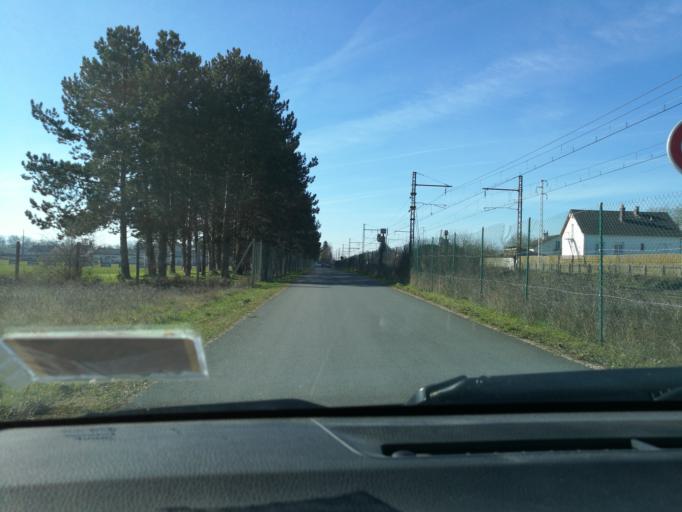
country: FR
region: Centre
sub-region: Departement du Loiret
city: Saint-Ay
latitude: 47.8654
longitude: 1.7549
